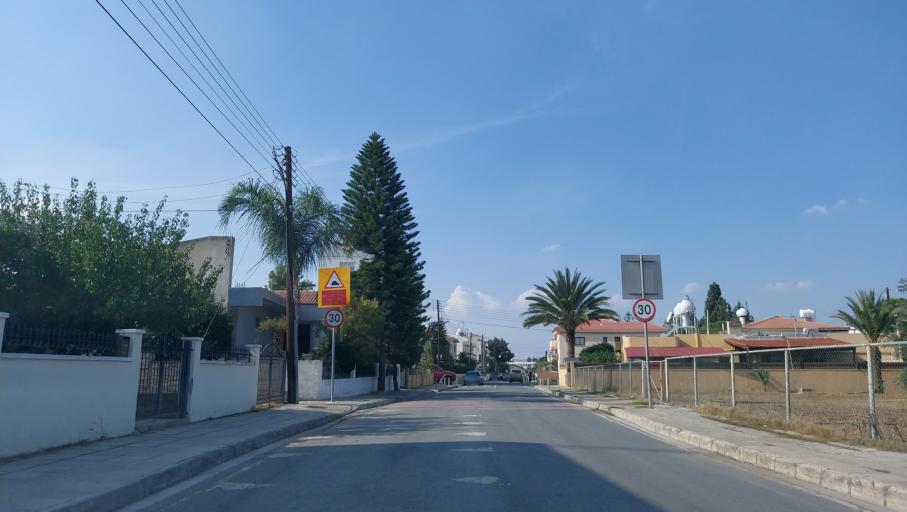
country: CY
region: Lefkosia
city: Tseri
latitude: 35.1087
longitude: 33.3073
